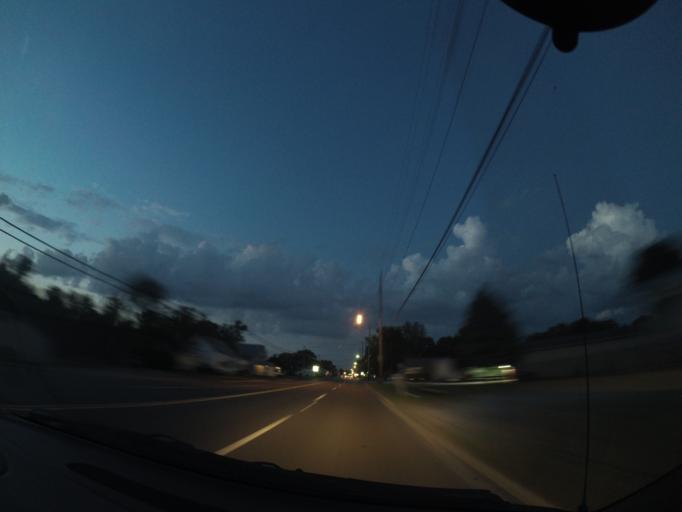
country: US
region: Ohio
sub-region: Ashtabula County
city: Ashtabula
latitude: 41.8505
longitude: -80.8241
